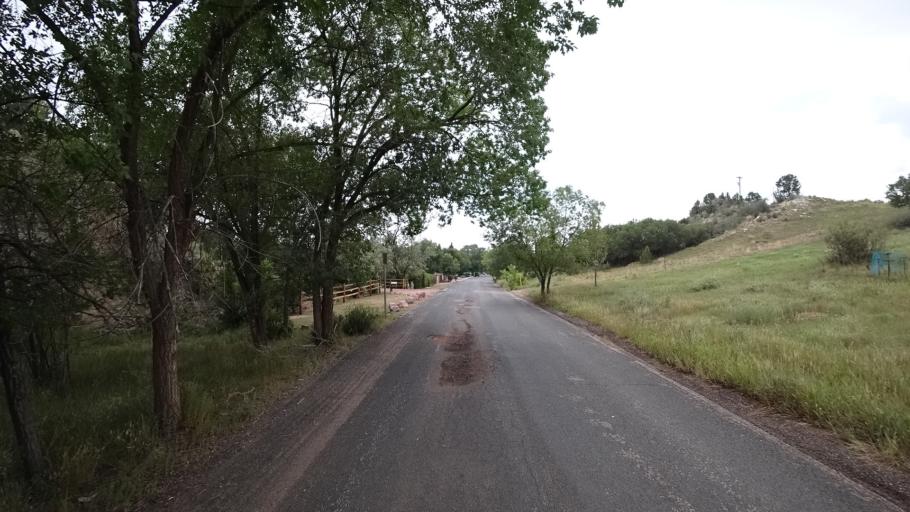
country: US
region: Colorado
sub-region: El Paso County
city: Manitou Springs
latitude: 38.8637
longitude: -104.8740
